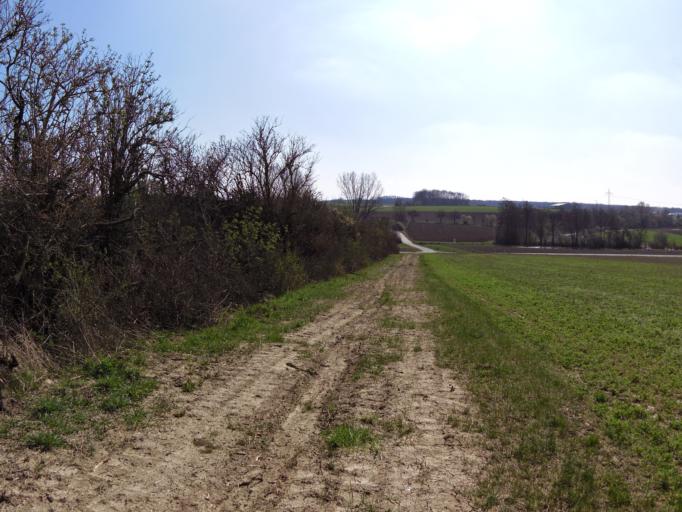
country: DE
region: Bavaria
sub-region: Regierungsbezirk Unterfranken
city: Biebelried
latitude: 49.7355
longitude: 10.0976
